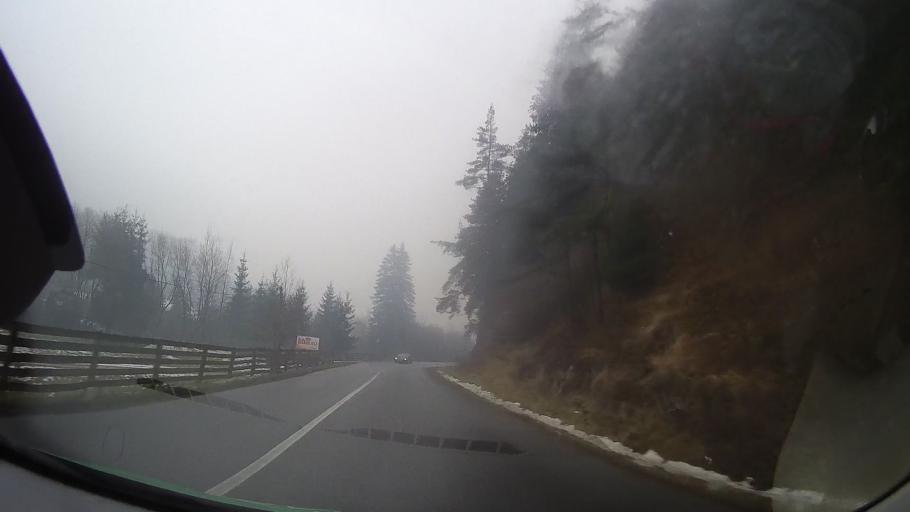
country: RO
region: Harghita
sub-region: Municipiul Gheorgheni
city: Gheorgheni
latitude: 46.7365
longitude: 25.6560
